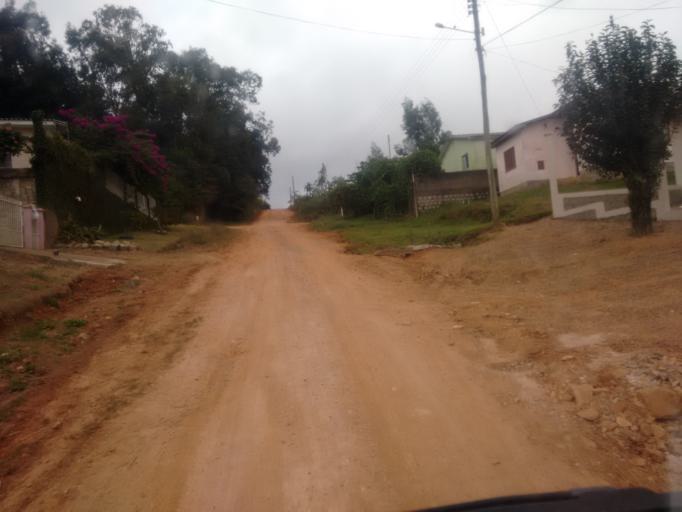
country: BR
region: Rio Grande do Sul
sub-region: Camaqua
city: Camaqua
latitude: -30.8348
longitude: -51.8172
